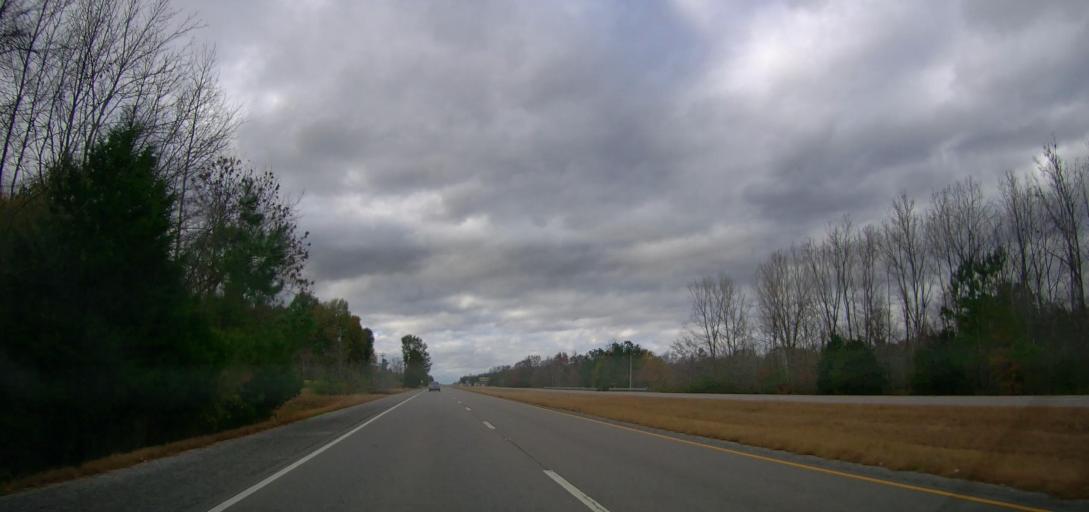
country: US
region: Alabama
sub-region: Lawrence County
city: Town Creek
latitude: 34.5839
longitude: -87.4158
